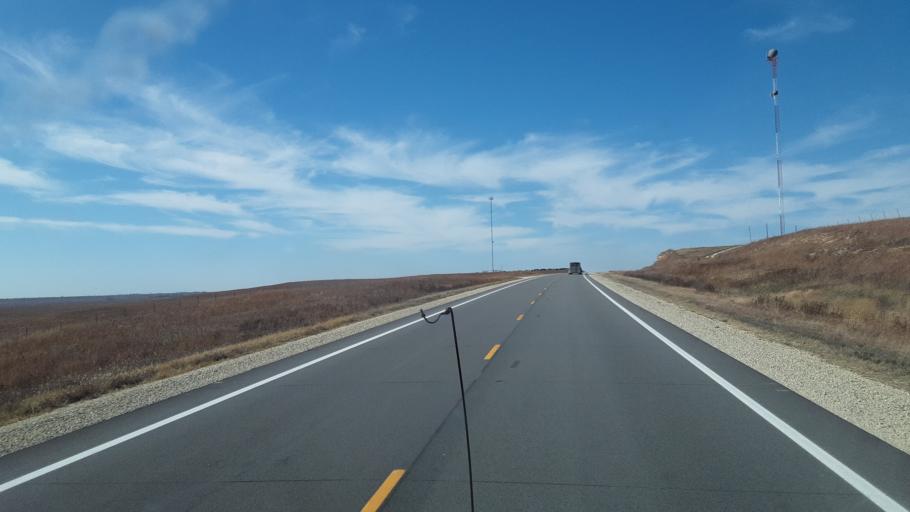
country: US
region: Kansas
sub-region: Chase County
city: Cottonwood Falls
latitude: 38.3626
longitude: -96.7291
